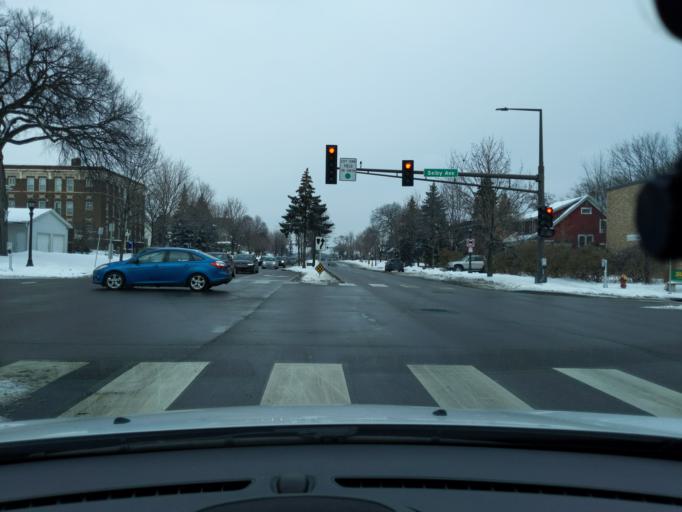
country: US
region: Minnesota
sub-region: Ramsey County
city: Falcon Heights
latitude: 44.9465
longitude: -93.1466
